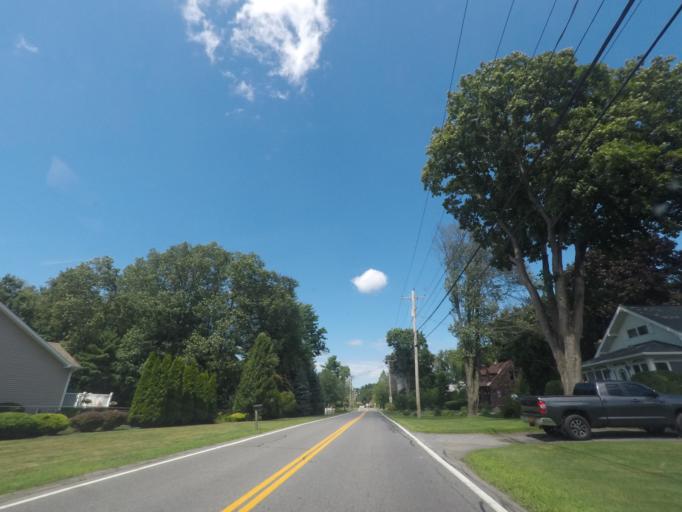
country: US
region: New York
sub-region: Schenectady County
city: Rotterdam
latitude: 42.7698
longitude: -73.9604
